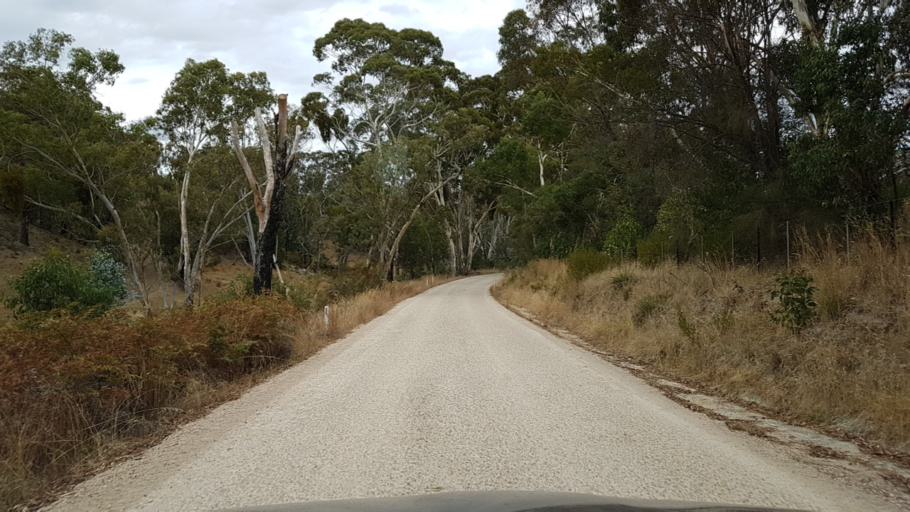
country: AU
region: South Australia
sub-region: Adelaide Hills
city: Gumeracha
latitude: -34.8007
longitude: 138.8211
